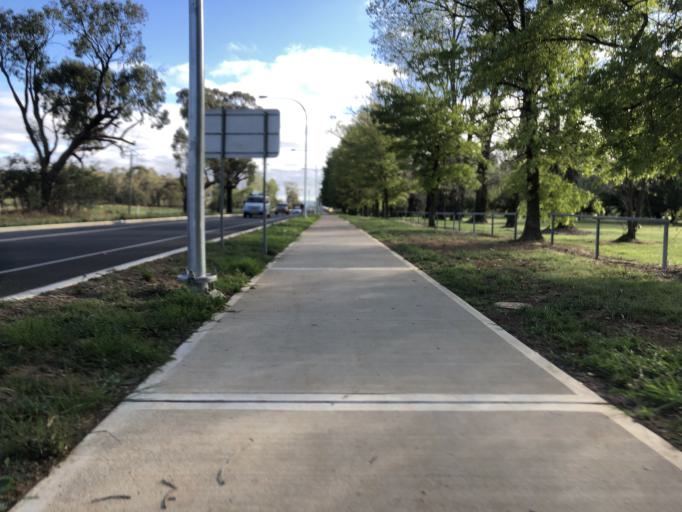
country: AU
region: New South Wales
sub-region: Orange Municipality
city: Orange
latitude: -33.3148
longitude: 149.0927
